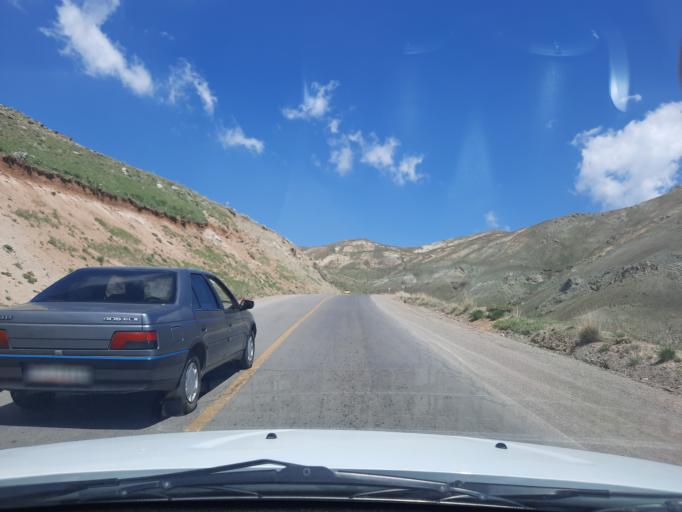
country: IR
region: Qazvin
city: Qazvin
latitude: 36.3765
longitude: 50.2109
